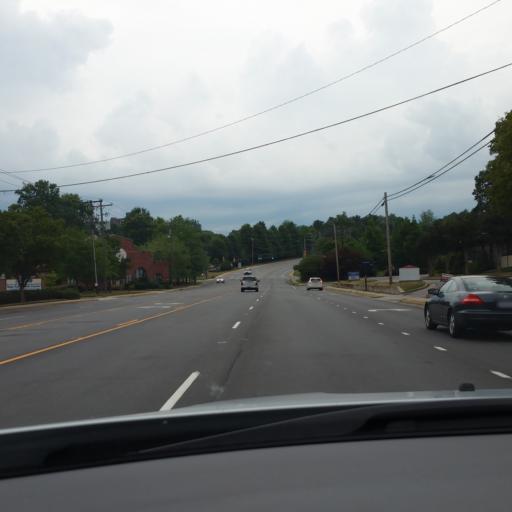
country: US
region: North Carolina
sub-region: Buncombe County
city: Asheville
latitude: 35.5831
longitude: -82.5549
